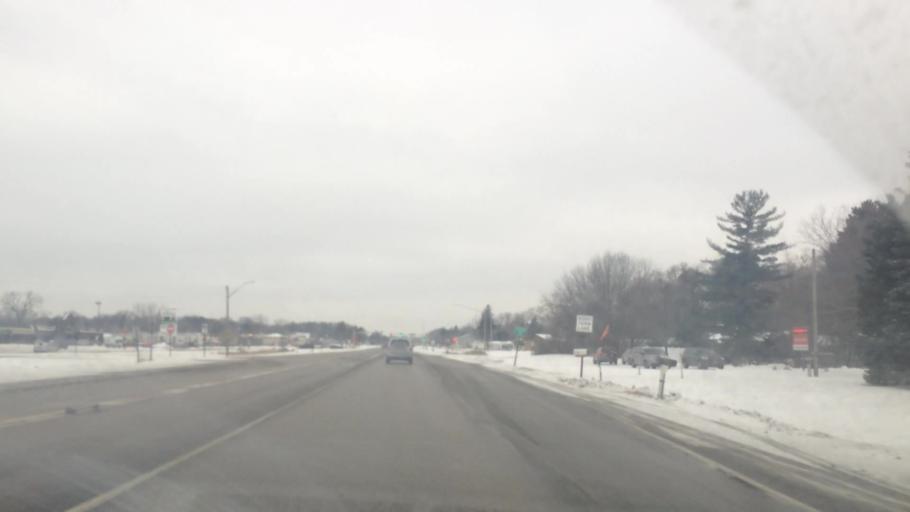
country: US
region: Minnesota
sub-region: Anoka County
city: Lexington
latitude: 45.1395
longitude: -93.1668
